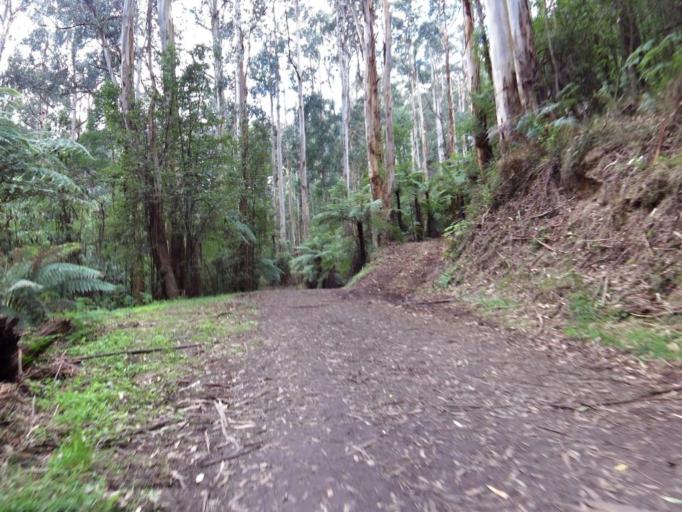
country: AU
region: Victoria
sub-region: Yarra Ranges
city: Ferny Creek
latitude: -37.8730
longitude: 145.3321
